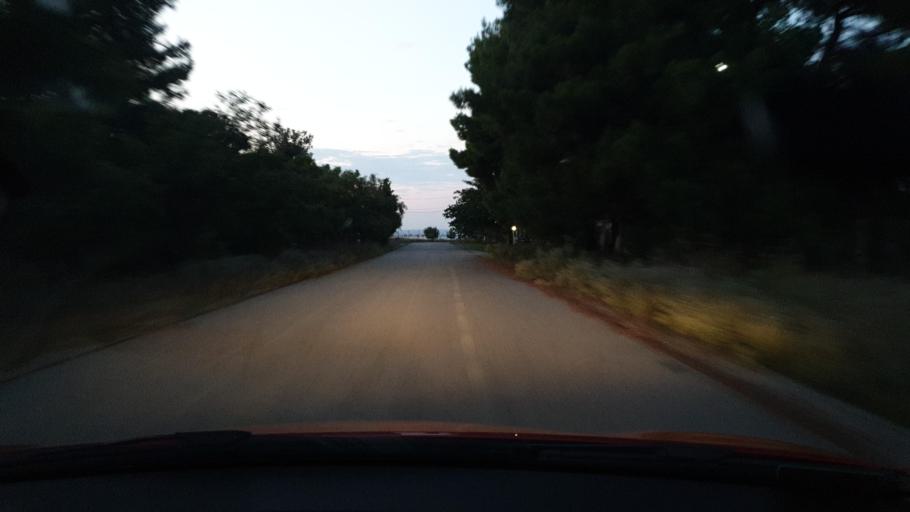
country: GR
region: Central Macedonia
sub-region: Nomos Thessalonikis
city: Agia Triada
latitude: 40.5050
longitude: 22.8324
